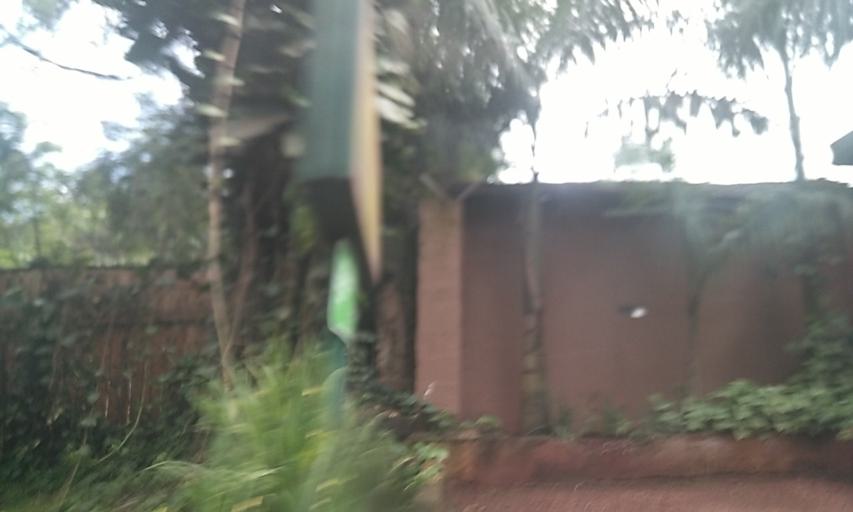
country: UG
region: Central Region
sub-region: Kampala District
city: Kampala
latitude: 0.3263
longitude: 32.5901
